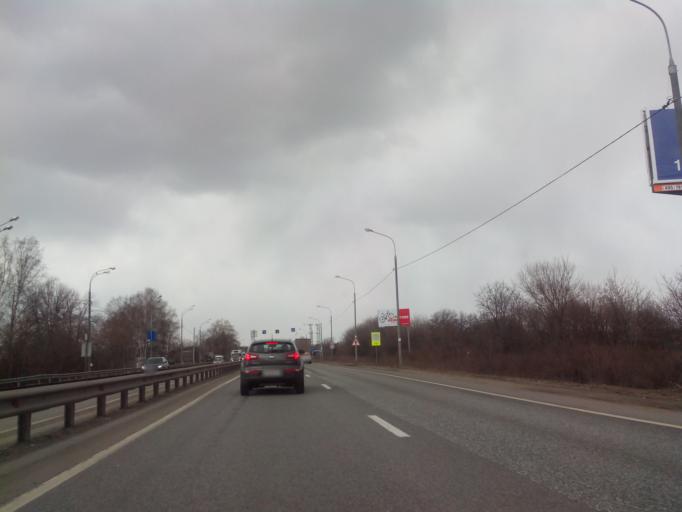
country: RU
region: Moskovskaya
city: Noginsk
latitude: 55.8338
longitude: 38.3912
